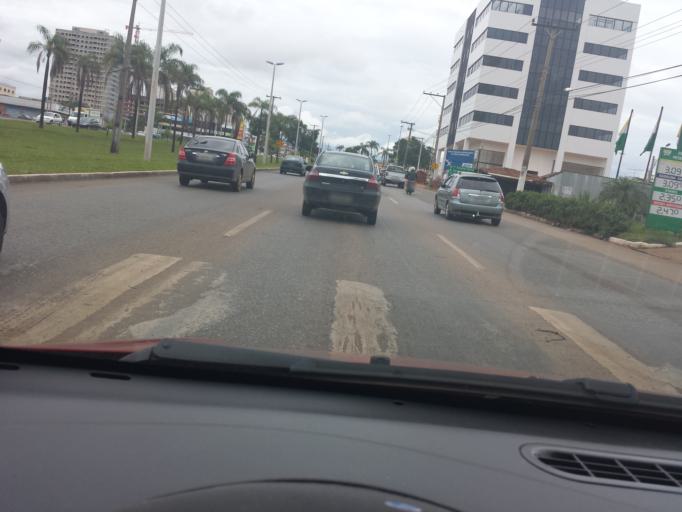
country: BR
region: Federal District
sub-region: Brasilia
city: Brasilia
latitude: -15.8517
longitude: -48.0728
